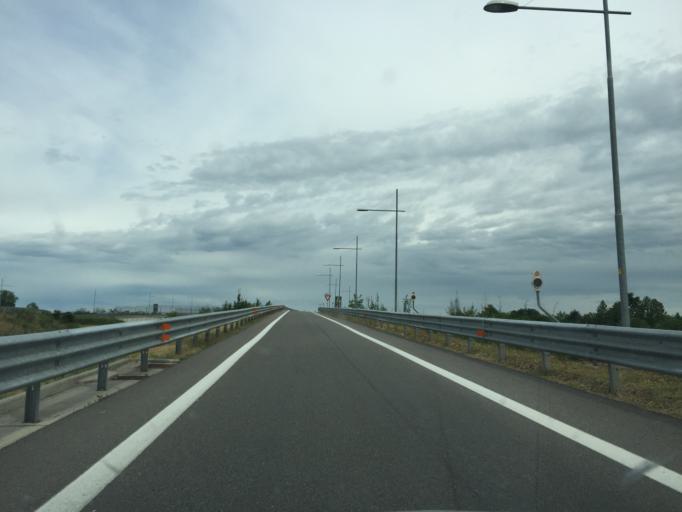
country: IT
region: Lombardy
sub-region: Provincia di Brescia
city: Borgosatollo
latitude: 45.4606
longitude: 10.2416
